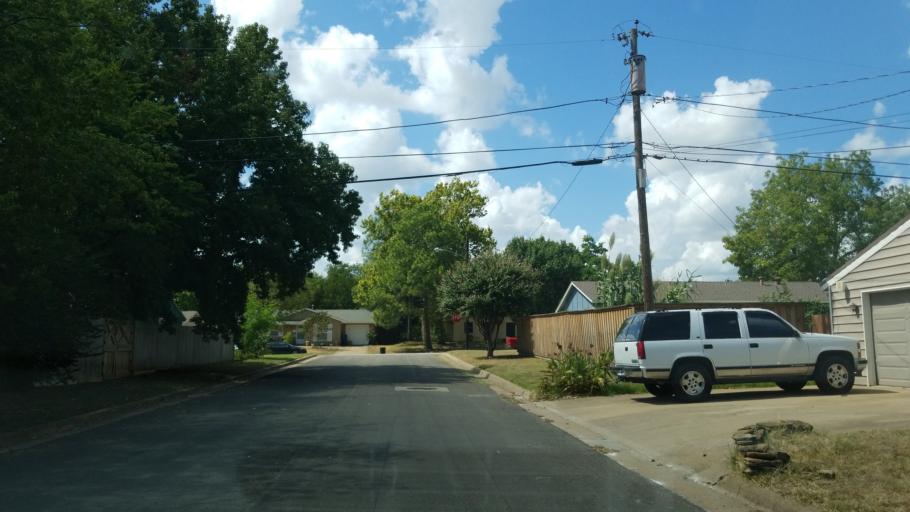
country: US
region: Texas
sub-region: Tarrant County
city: Euless
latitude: 32.8550
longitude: -97.0915
